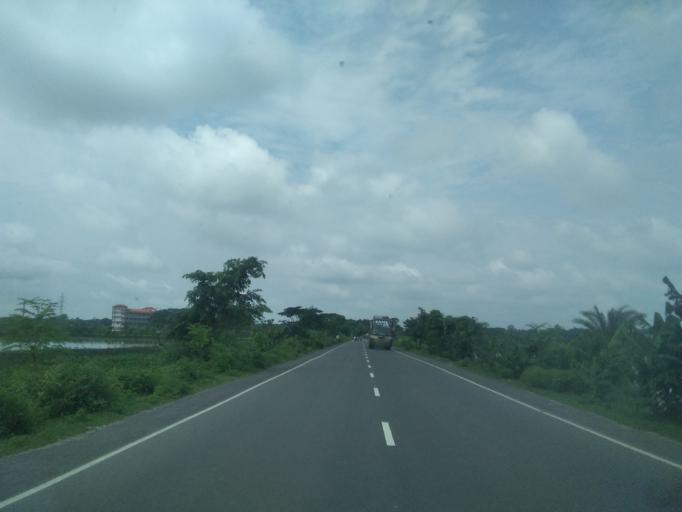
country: BD
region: Khulna
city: Kesabpur
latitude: 22.8094
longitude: 89.2423
